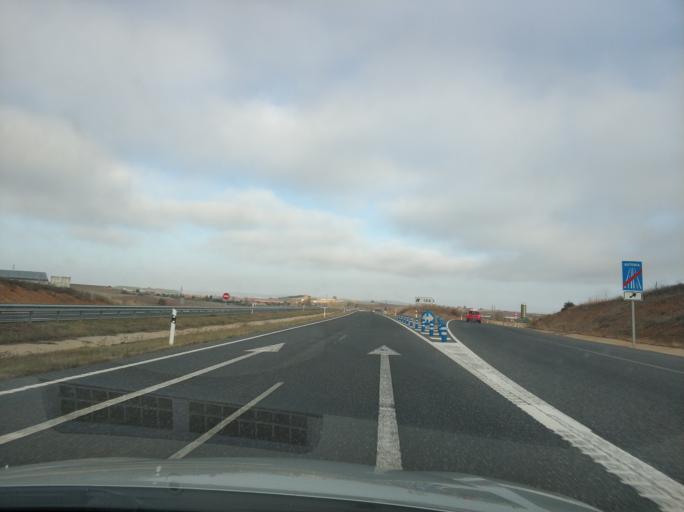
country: ES
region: Castille and Leon
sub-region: Provincia de Leon
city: Valdefresno
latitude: 42.5624
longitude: -5.4926
